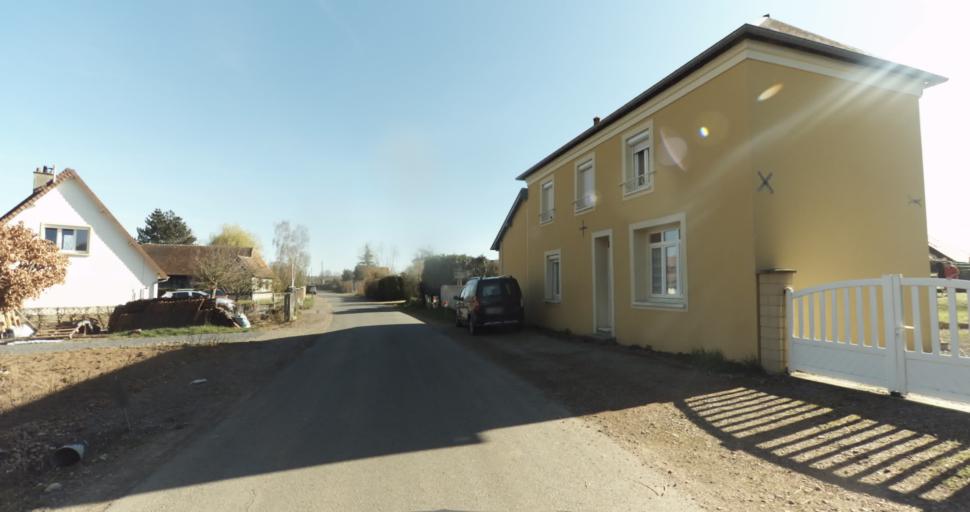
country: FR
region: Lower Normandy
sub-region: Departement du Calvados
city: Saint-Pierre-sur-Dives
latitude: 49.0360
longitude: 0.0521
